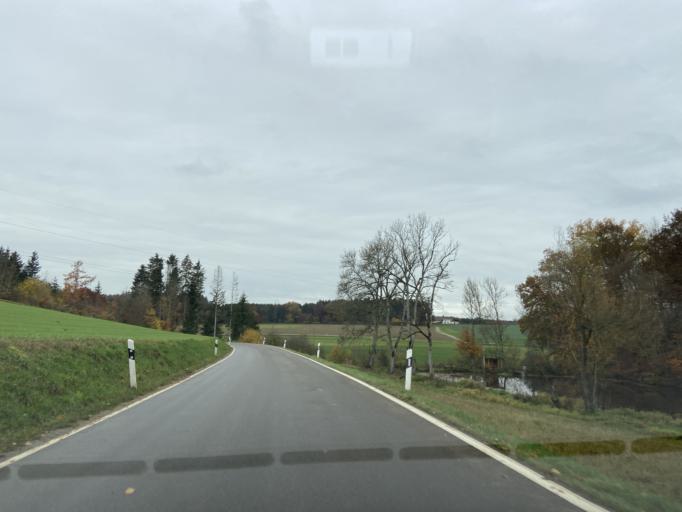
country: DE
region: Baden-Wuerttemberg
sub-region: Tuebingen Region
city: Wald
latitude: 47.9721
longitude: 9.1612
